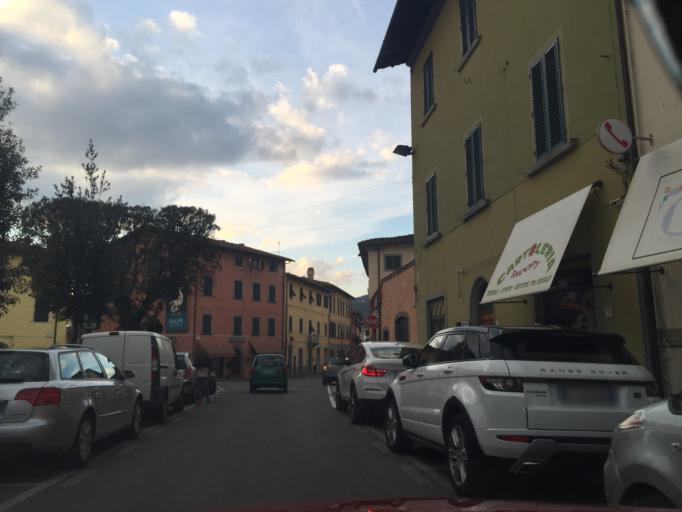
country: IT
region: Tuscany
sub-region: Provincia di Pistoia
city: Borgo a Buggiano
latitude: 43.8781
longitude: 10.7312
